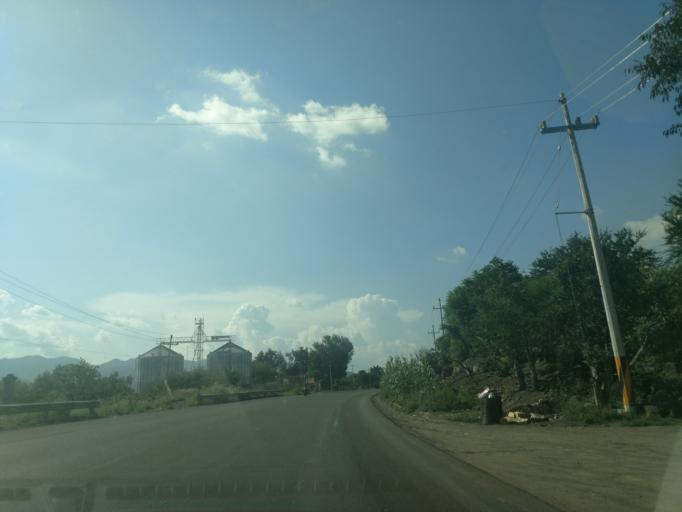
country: MX
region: Jalisco
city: Ahualulco de Mercado
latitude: 20.6970
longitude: -103.9634
